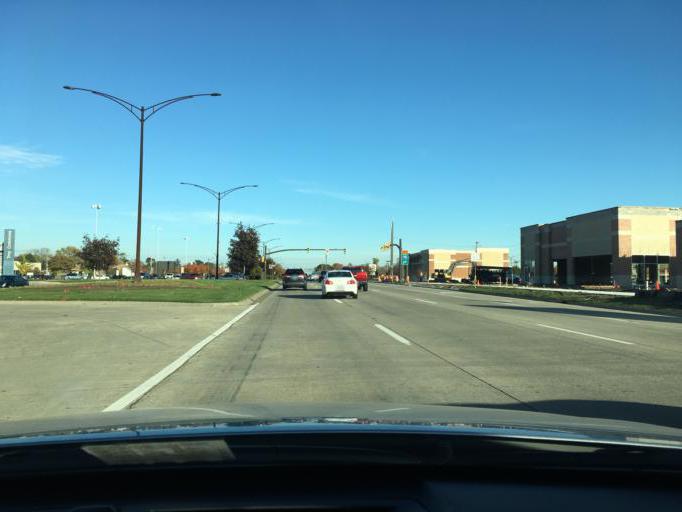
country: US
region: Michigan
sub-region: Oakland County
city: Clawson
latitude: 42.5628
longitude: -83.1327
